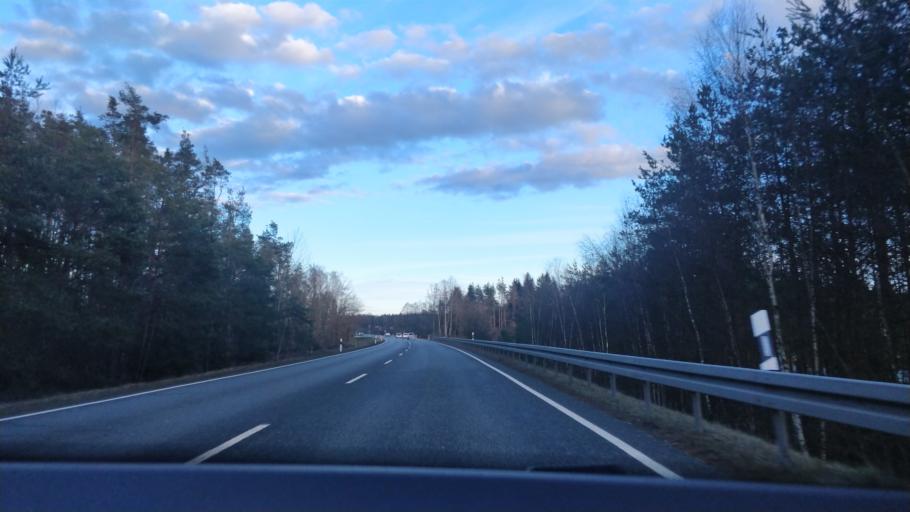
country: DE
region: Bavaria
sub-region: Upper Palatinate
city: Schwarzenbach
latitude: 49.7218
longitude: 11.9750
